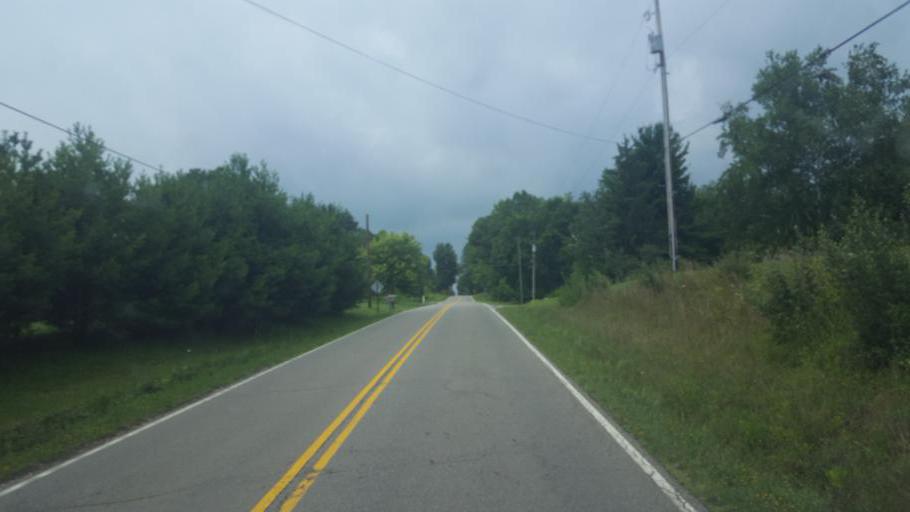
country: US
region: Ohio
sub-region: Licking County
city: Granville
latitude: 40.1456
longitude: -82.4832
